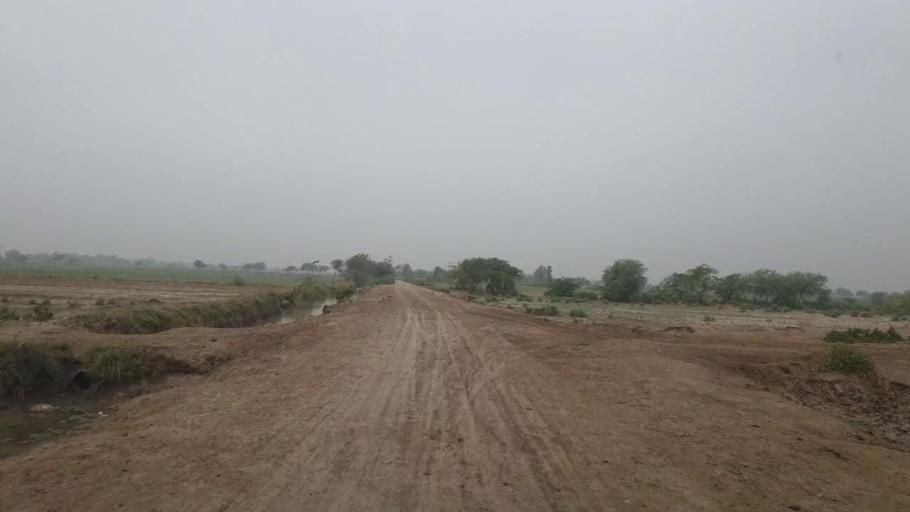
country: PK
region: Sindh
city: Badin
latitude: 24.5708
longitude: 68.6605
